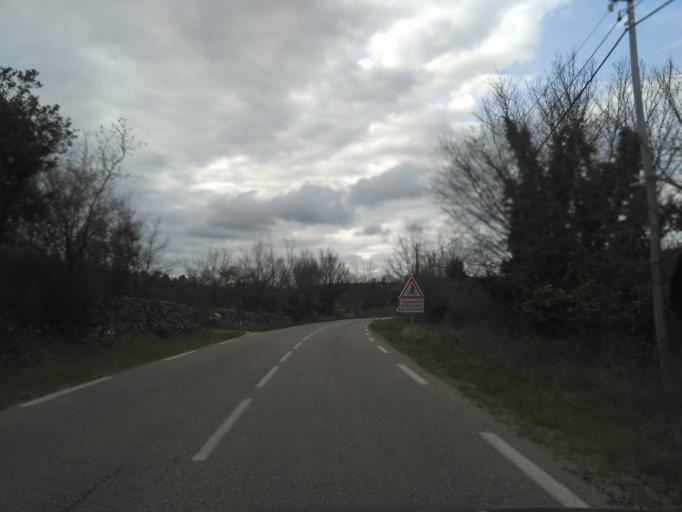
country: FR
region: Provence-Alpes-Cote d'Azur
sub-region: Departement du Var
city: Barjols
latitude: 43.5777
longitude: 6.0160
